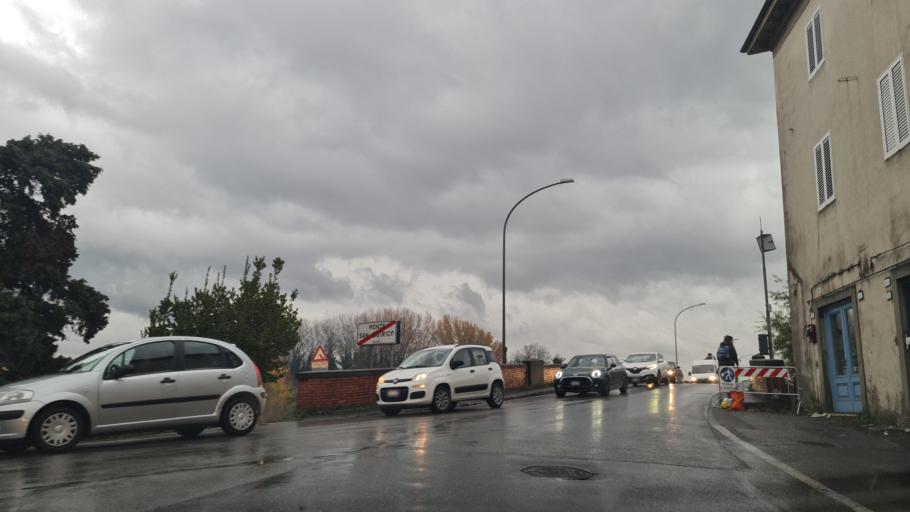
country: IT
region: Tuscany
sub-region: Provincia di Lucca
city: Lucca
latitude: 43.8580
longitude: 10.5058
